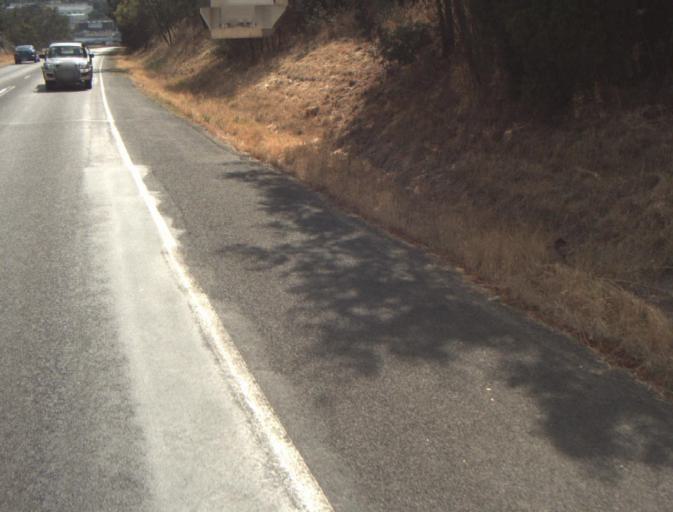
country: AU
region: Tasmania
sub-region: Launceston
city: Summerhill
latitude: -41.4803
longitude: 147.1581
